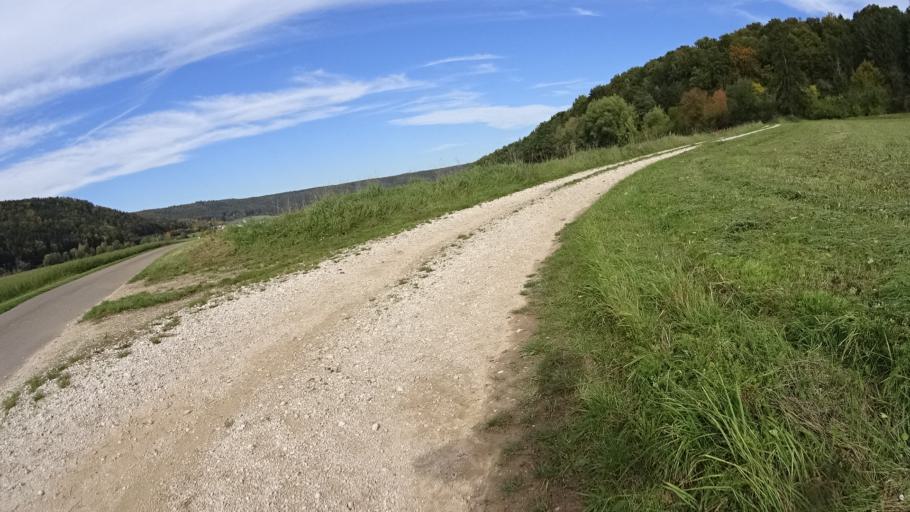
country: DE
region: Bavaria
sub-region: Upper Bavaria
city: Walting
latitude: 48.9174
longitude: 11.3064
